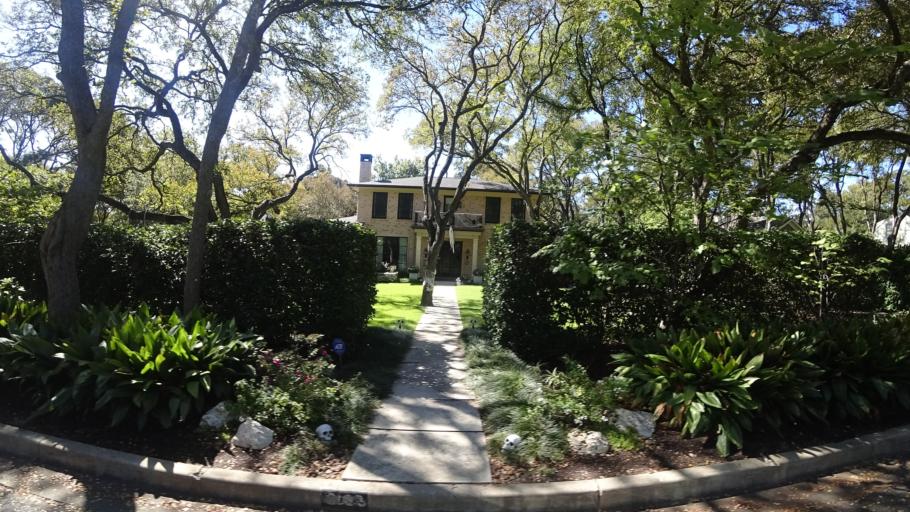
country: US
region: Texas
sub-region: Travis County
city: Rollingwood
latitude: 30.2909
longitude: -97.7643
